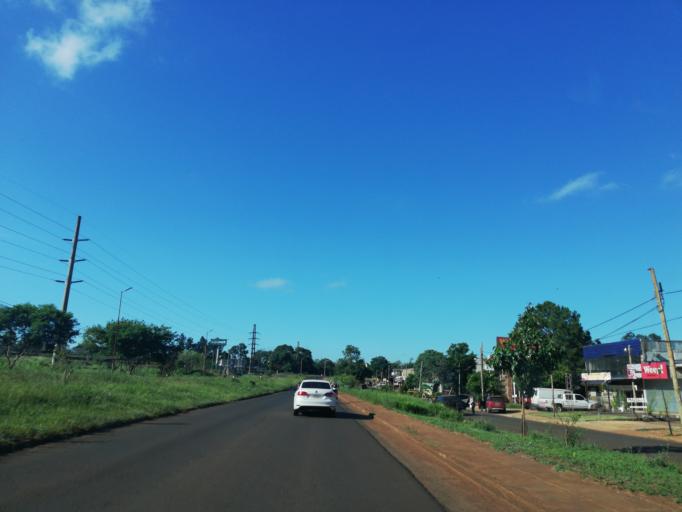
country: AR
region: Misiones
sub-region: Departamento de Capital
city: Posadas
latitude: -27.4230
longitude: -55.9330
